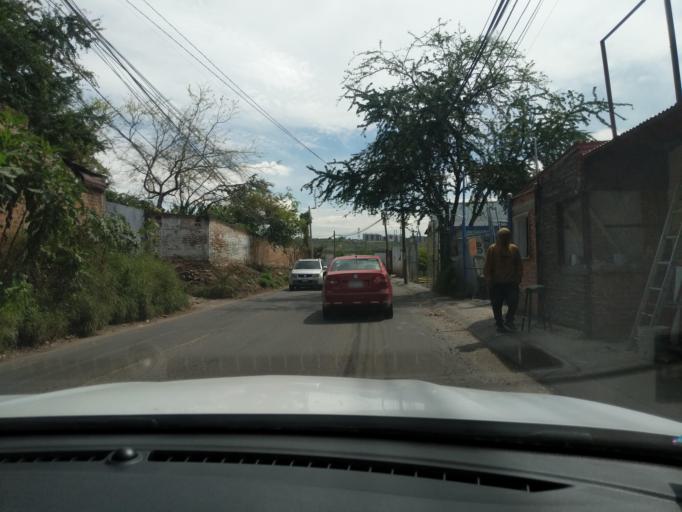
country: MX
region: Jalisco
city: Tonala
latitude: 20.6488
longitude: -103.2275
